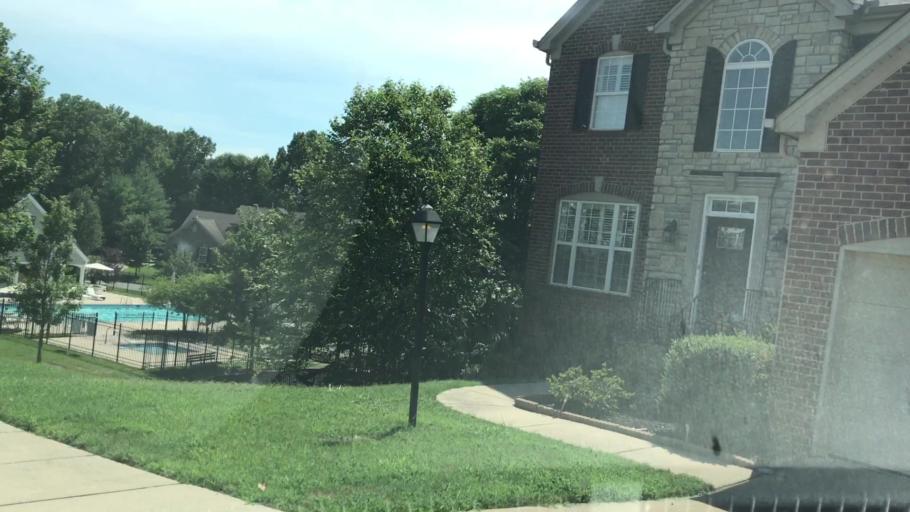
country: US
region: Tennessee
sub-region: Williamson County
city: Brentwood Estates
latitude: 36.0169
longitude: -86.7125
